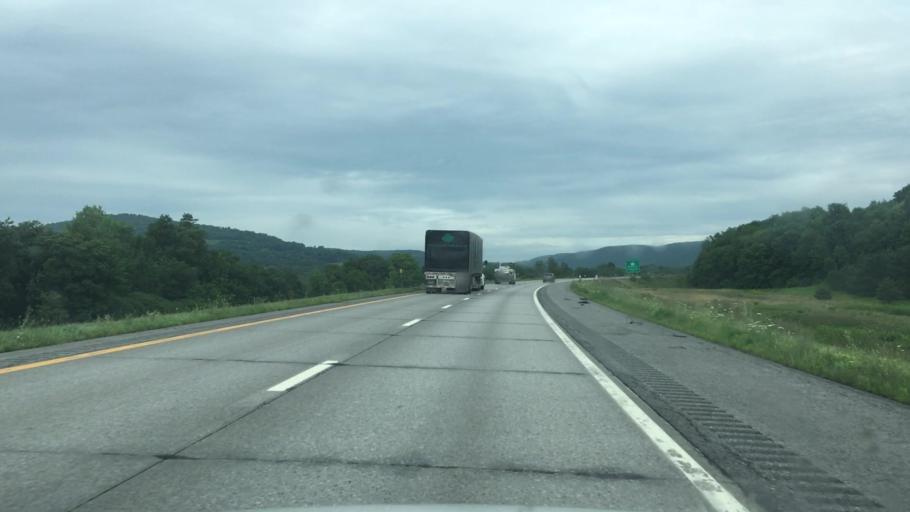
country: US
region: New York
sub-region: Otsego County
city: Worcester
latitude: 42.5849
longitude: -74.7565
